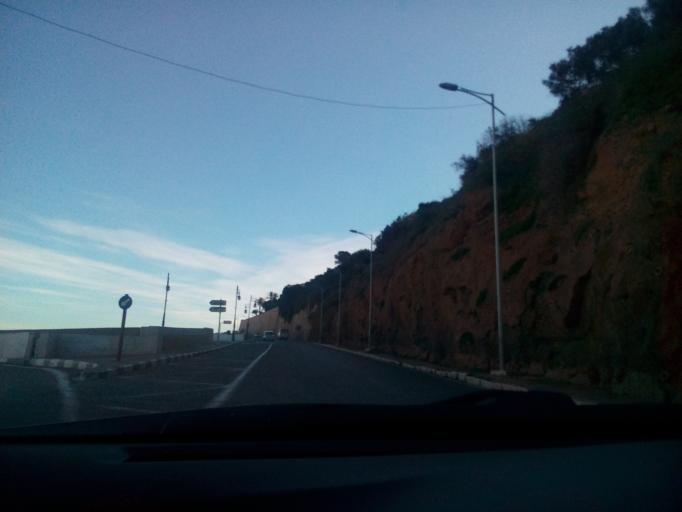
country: DZ
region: Oran
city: Oran
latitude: 35.7074
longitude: -0.6492
